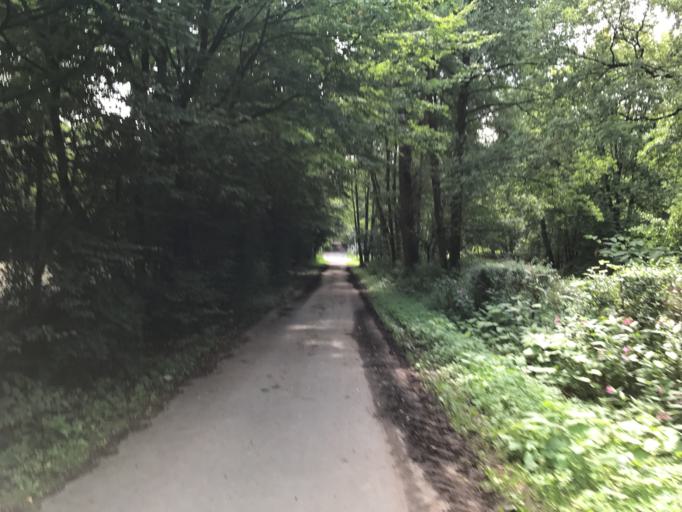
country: DE
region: North Rhine-Westphalia
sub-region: Regierungsbezirk Dusseldorf
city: Duisburg
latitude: 51.4172
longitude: 6.8165
